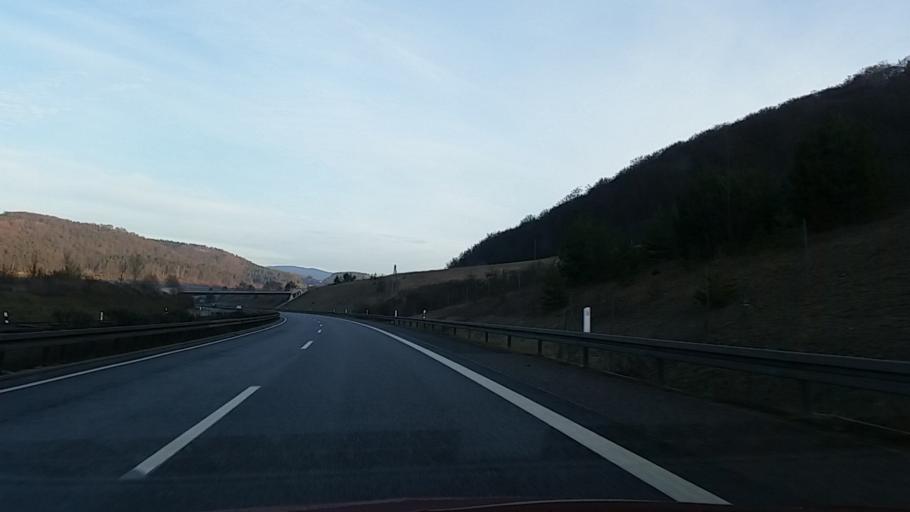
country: DE
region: Thuringia
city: Ellingshausen
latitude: 50.5449
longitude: 10.4793
